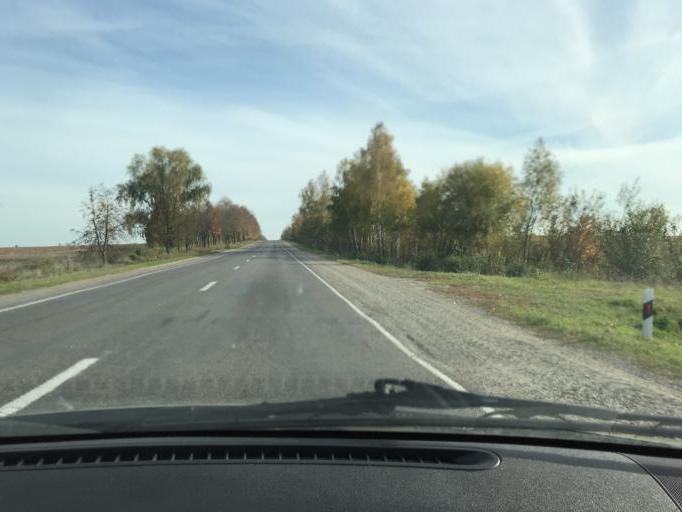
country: BY
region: Brest
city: Asnyezhytsy
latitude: 52.2179
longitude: 26.0370
